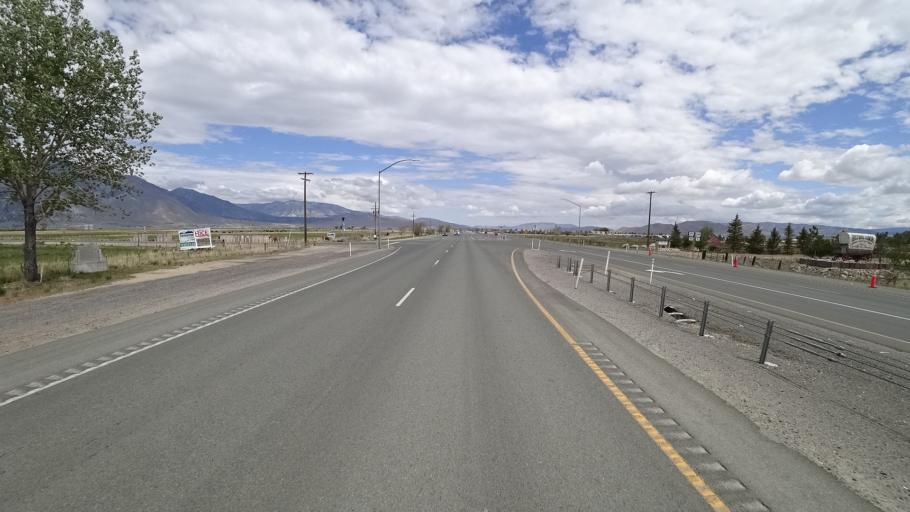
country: US
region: Nevada
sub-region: Douglas County
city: Minden
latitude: 38.9960
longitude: -119.7797
